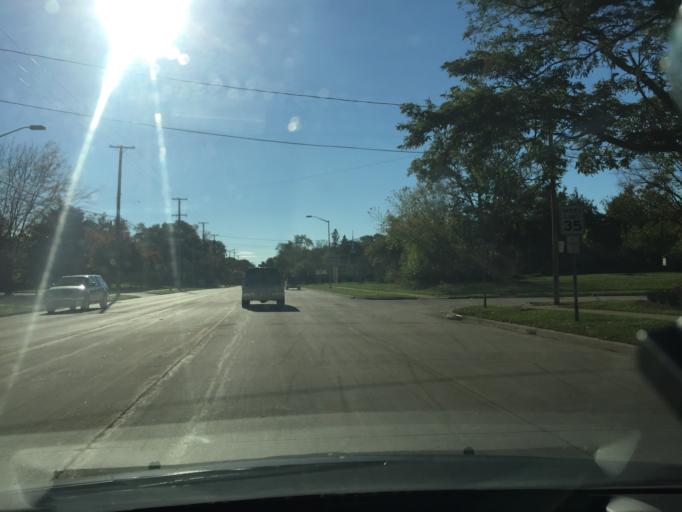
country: US
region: Michigan
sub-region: Oakland County
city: Pontiac
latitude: 42.6467
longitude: -83.2750
